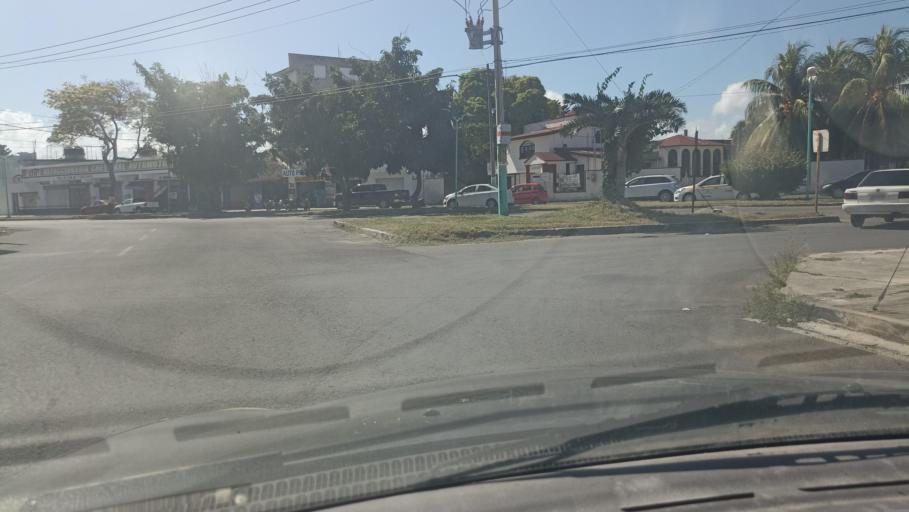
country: MX
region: Quintana Roo
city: Chetumal
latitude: 18.5076
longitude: -88.2921
